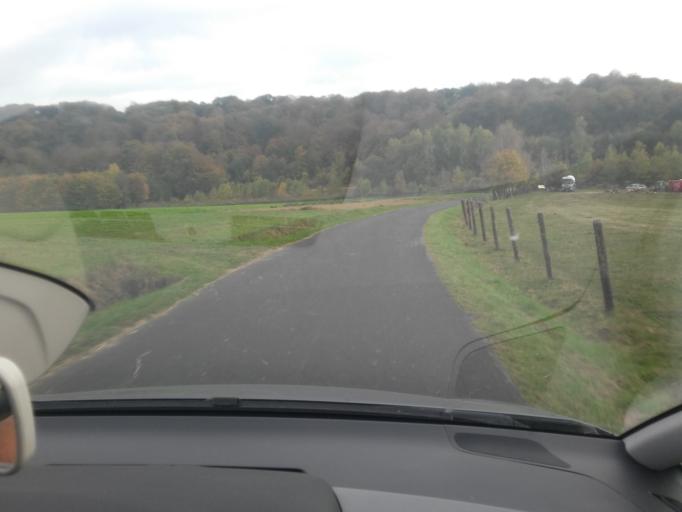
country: BE
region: Wallonia
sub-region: Province du Luxembourg
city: Attert
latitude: 49.7234
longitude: 5.7694
